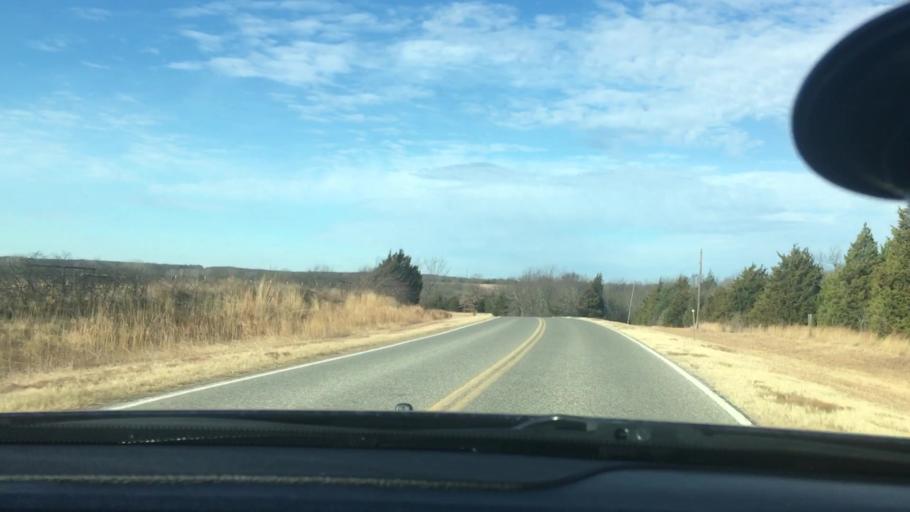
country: US
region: Oklahoma
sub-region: Seminole County
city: Konawa
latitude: 34.9848
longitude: -96.7973
